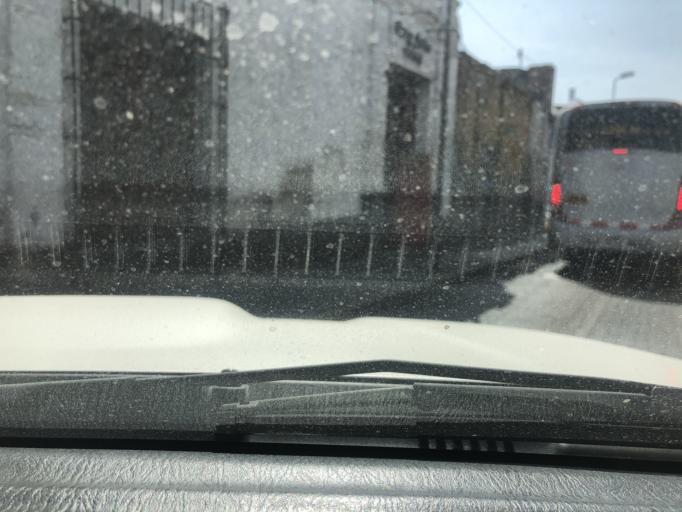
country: PE
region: Arequipa
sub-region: Provincia de Arequipa
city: Arequipa
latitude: -16.3954
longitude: -71.5313
